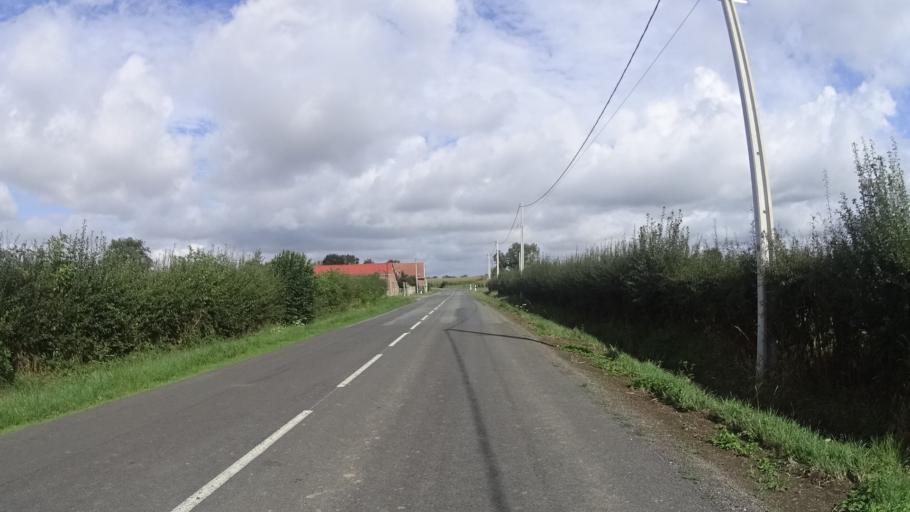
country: FR
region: Nord-Pas-de-Calais
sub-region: Departement du Nord
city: Landrecies
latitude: 50.0807
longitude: 3.6494
